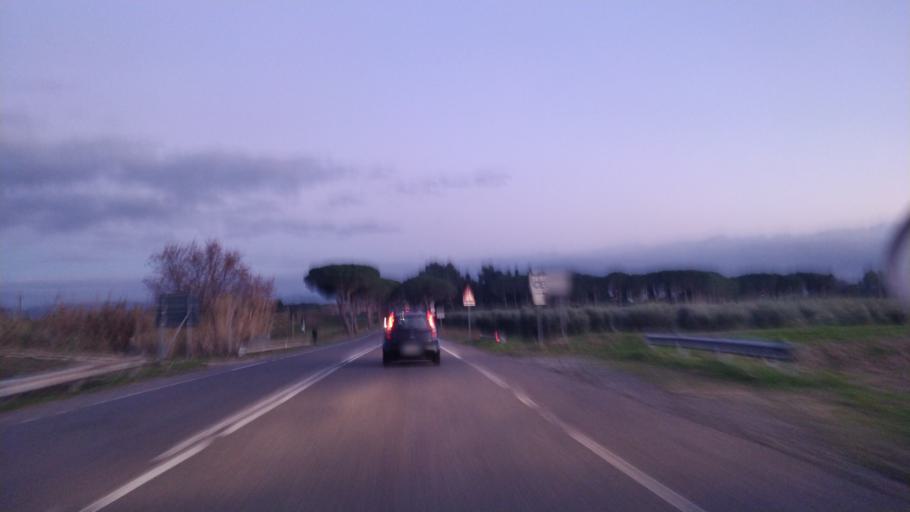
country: IT
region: Tuscany
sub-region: Provincia di Livorno
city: S.P. in Palazzi
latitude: 43.3356
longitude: 10.4898
